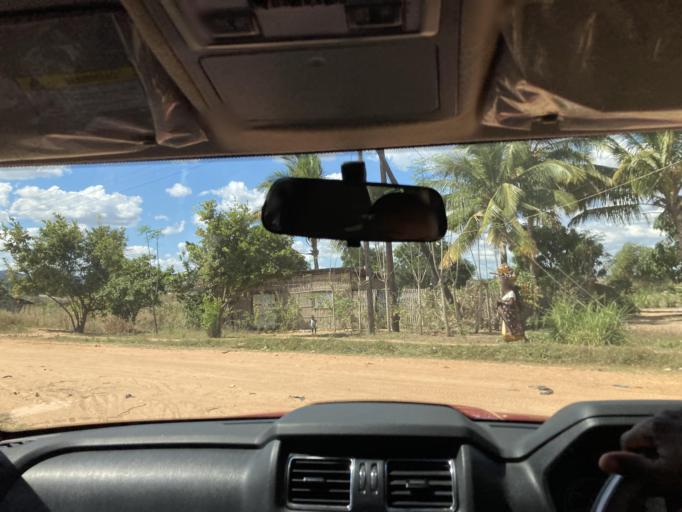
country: MZ
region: Cabo Delgado
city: Montepuez
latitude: -13.1496
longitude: 38.9910
